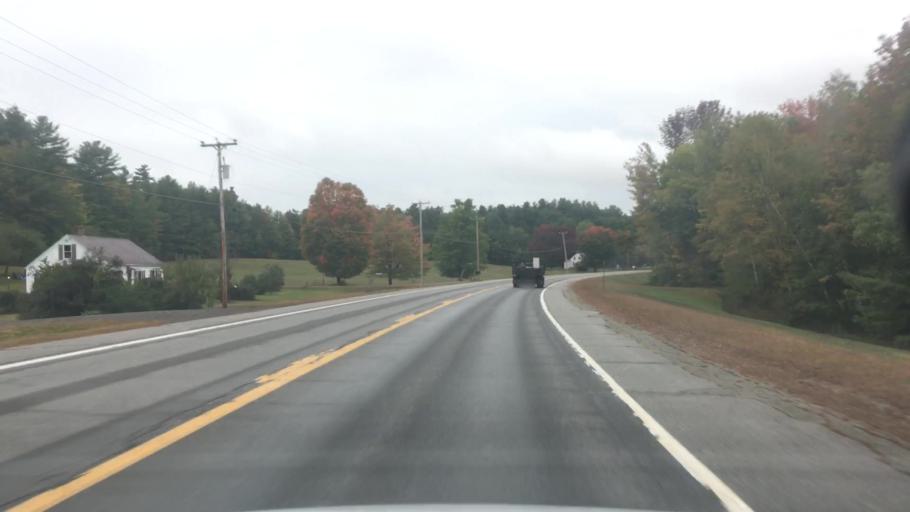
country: US
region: Maine
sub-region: Kennebec County
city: Belgrade
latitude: 44.4340
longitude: -69.8330
